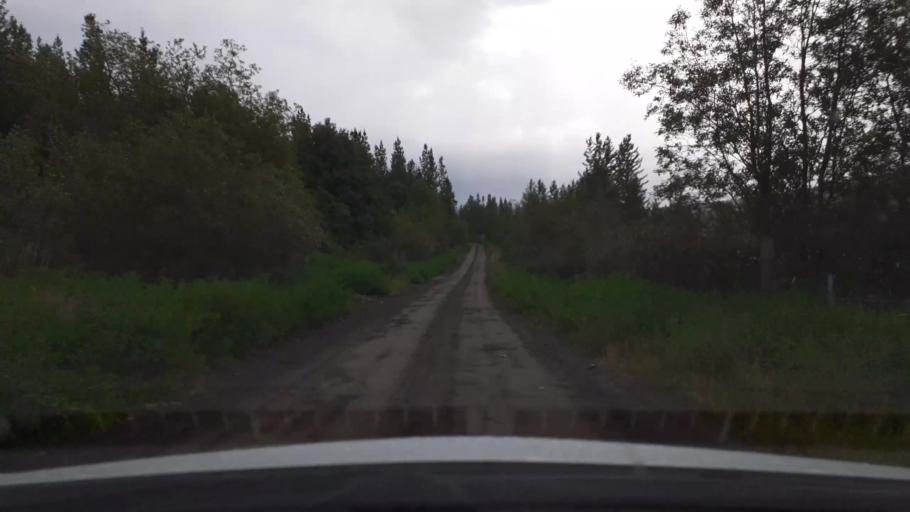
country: IS
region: Capital Region
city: Mosfellsbaer
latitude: 64.4967
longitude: -21.3565
